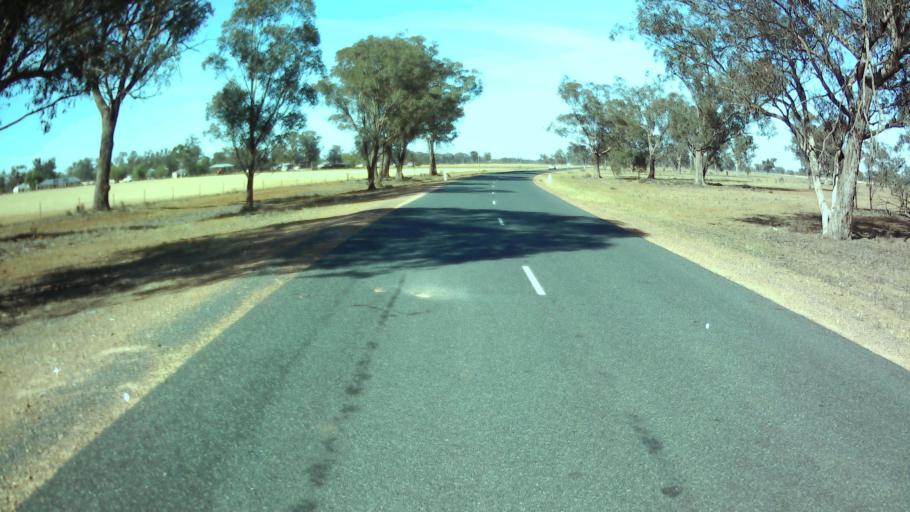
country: AU
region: New South Wales
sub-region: Weddin
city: Grenfell
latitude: -34.0974
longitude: 147.8837
